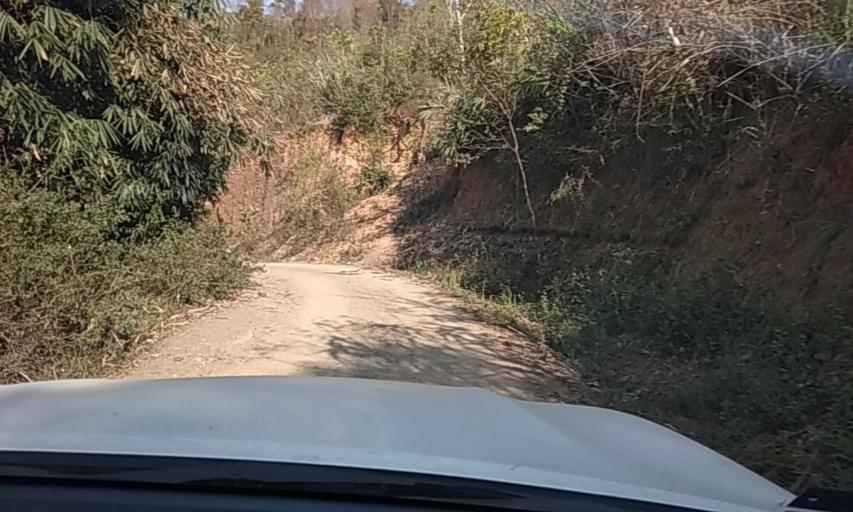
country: LA
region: Phongsali
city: Phongsali
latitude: 21.6939
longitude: 102.0935
